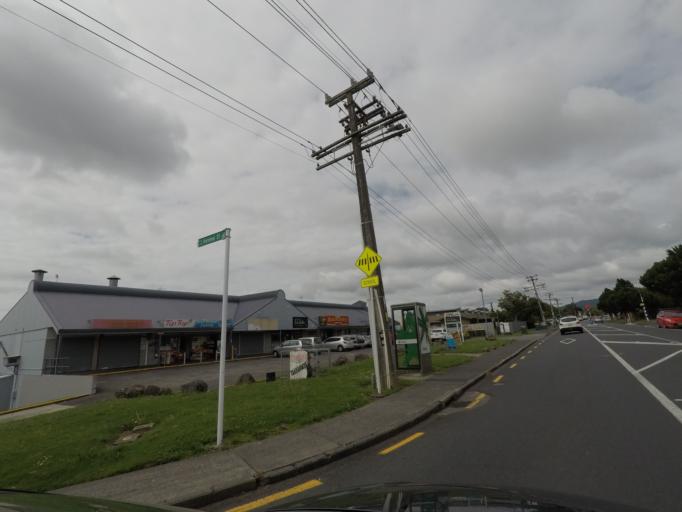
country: NZ
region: Auckland
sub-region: Auckland
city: Waitakere
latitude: -36.8952
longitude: 174.6277
